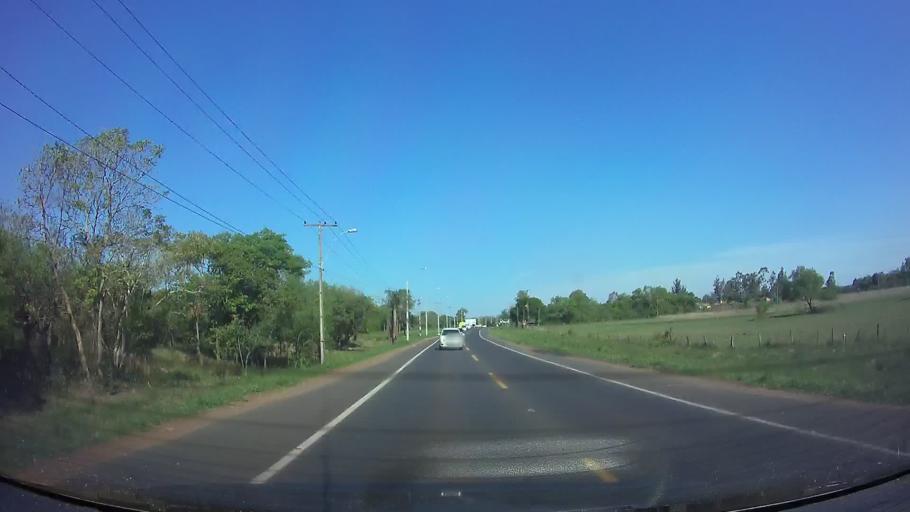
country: PY
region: Central
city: Itaugua
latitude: -25.3448
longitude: -57.3411
